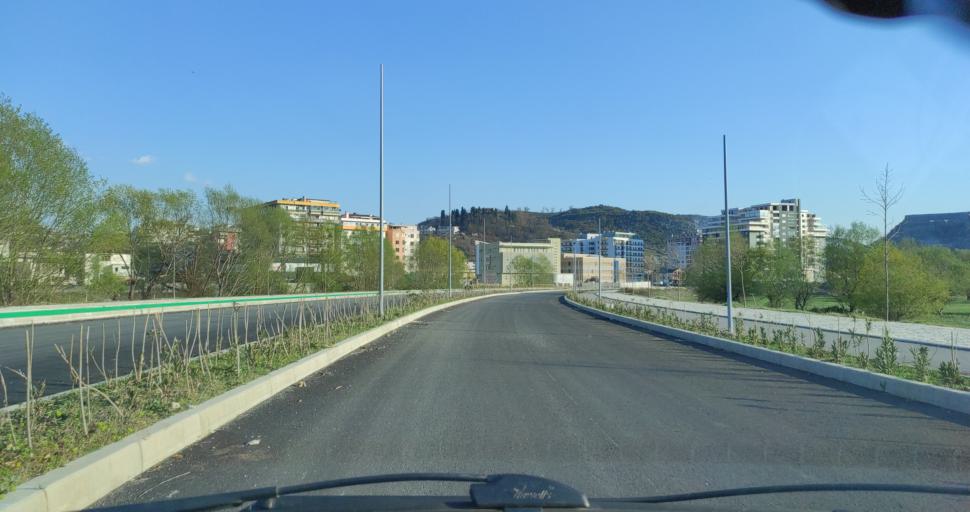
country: AL
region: Shkoder
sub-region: Rrethi i Shkodres
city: Shkoder
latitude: 42.0587
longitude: 19.4979
